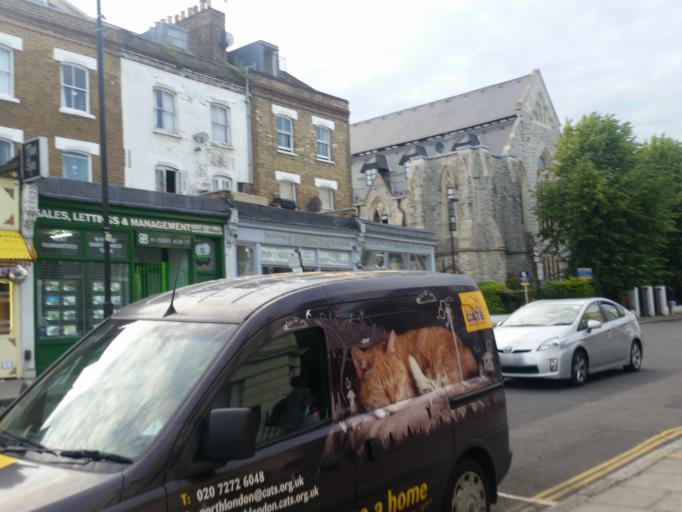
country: GB
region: England
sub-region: Greater London
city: Holloway
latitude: 51.5611
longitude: -0.1367
